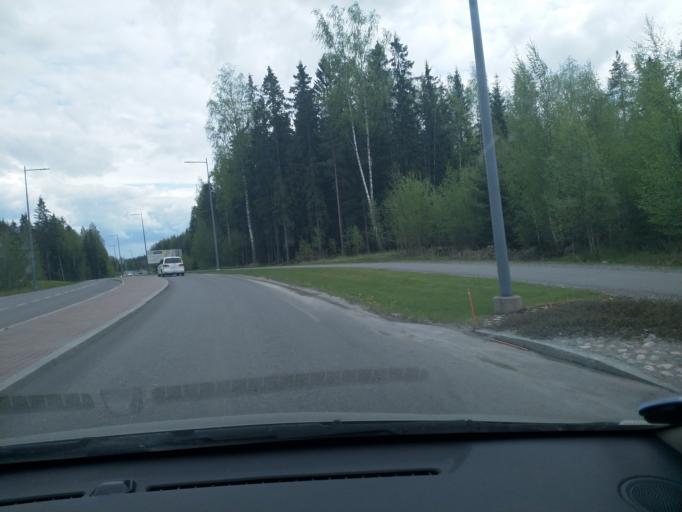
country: FI
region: Pirkanmaa
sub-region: Tampere
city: Tampere
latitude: 61.4552
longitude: 23.7947
